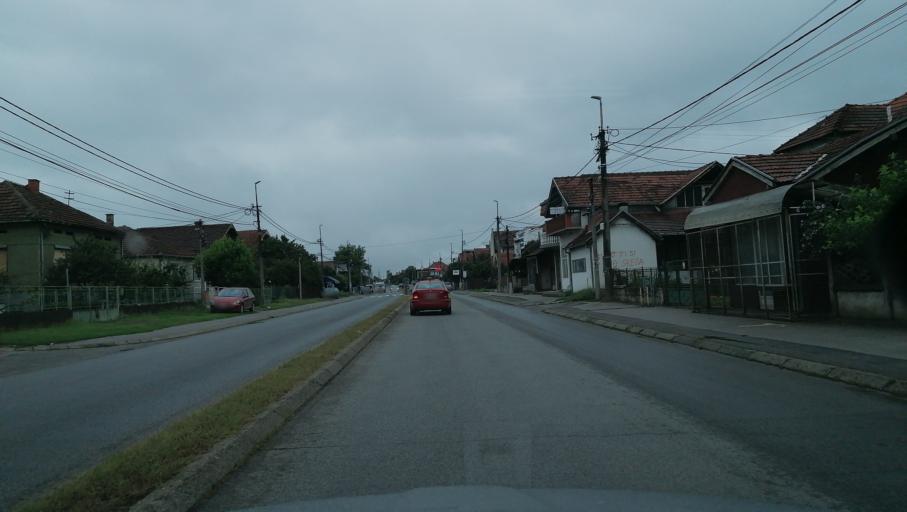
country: RS
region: Central Serbia
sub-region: Rasinski Okrug
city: Krusevac
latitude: 43.5854
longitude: 21.3004
